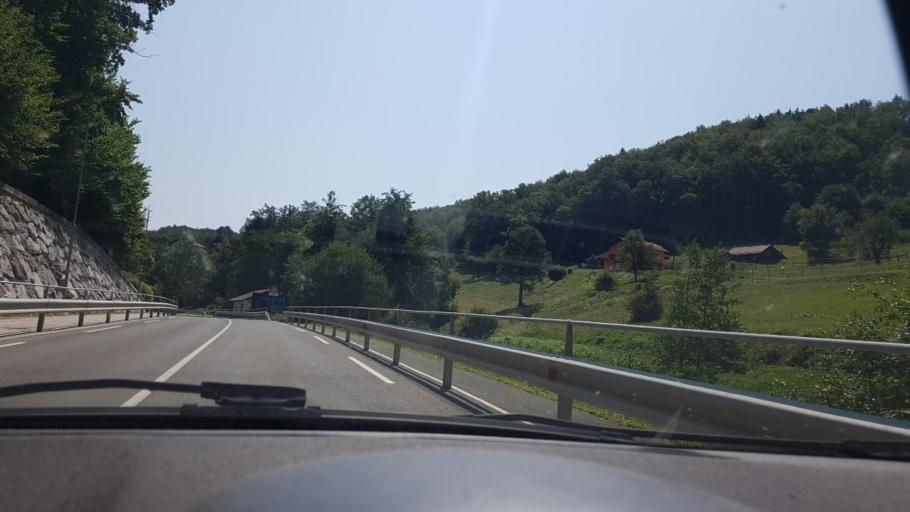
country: SI
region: Rogaska Slatina
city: Rogaska Slatina
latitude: 46.2392
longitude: 15.6063
